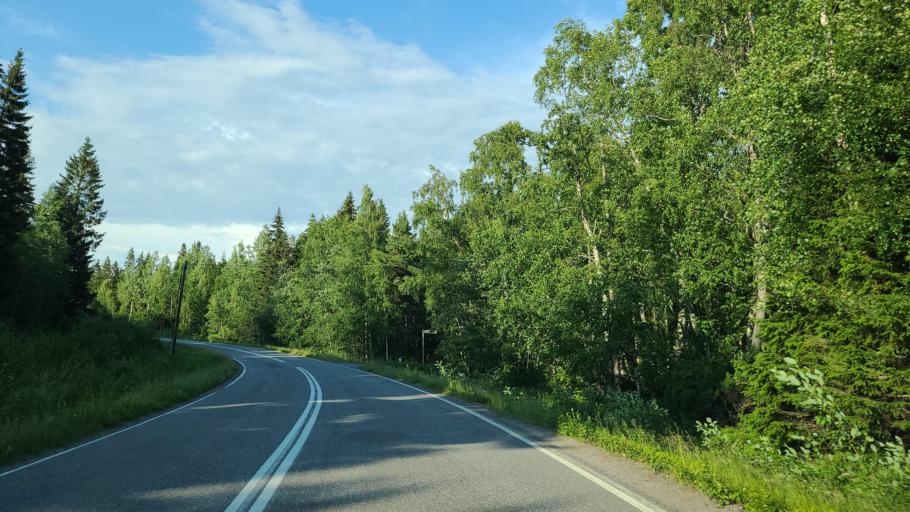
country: FI
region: Ostrobothnia
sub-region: Vaasa
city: Replot
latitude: 63.2918
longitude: 21.3537
